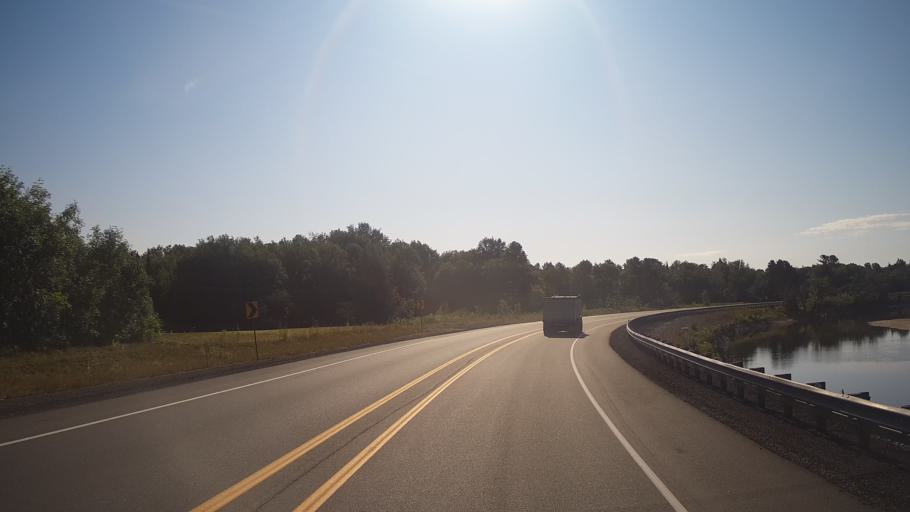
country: CA
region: Ontario
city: Elliot Lake
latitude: 46.2077
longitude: -83.0278
